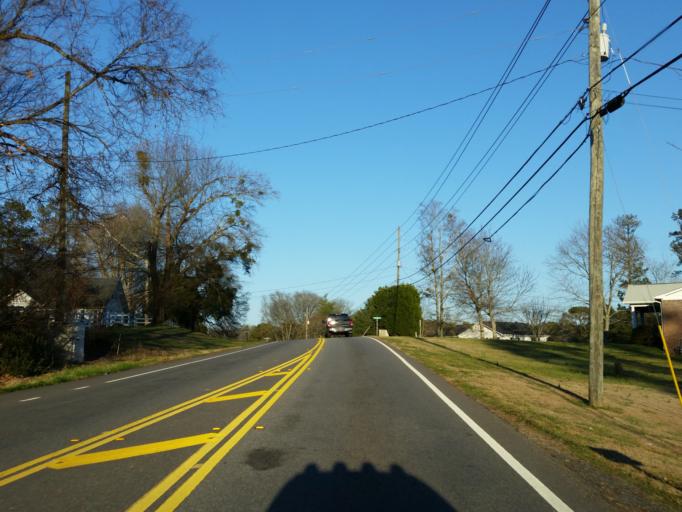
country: US
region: Georgia
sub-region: Cherokee County
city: Holly Springs
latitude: 34.1329
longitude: -84.4801
